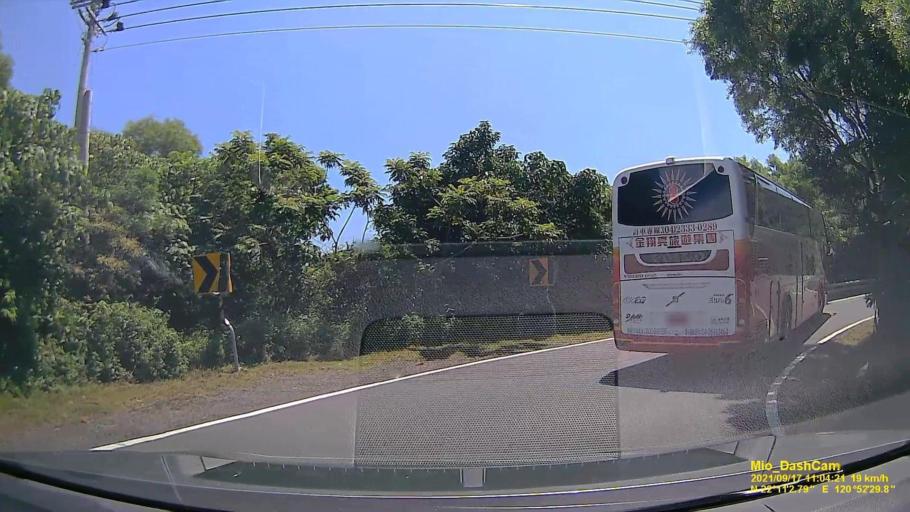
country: TW
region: Taiwan
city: Hengchun
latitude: 22.1841
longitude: 120.8750
